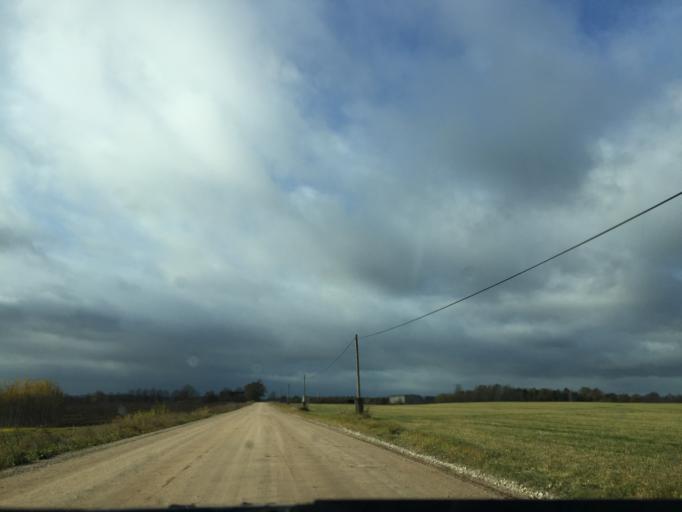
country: LV
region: Tukuma Rajons
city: Tukums
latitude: 56.9725
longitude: 23.0874
